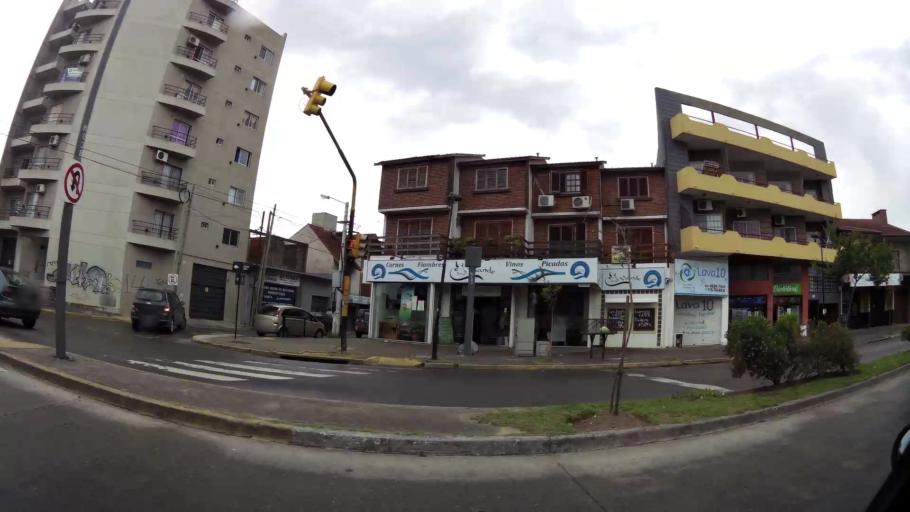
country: AR
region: Buenos Aires
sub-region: Partido de Quilmes
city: Quilmes
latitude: -34.7551
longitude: -58.2098
